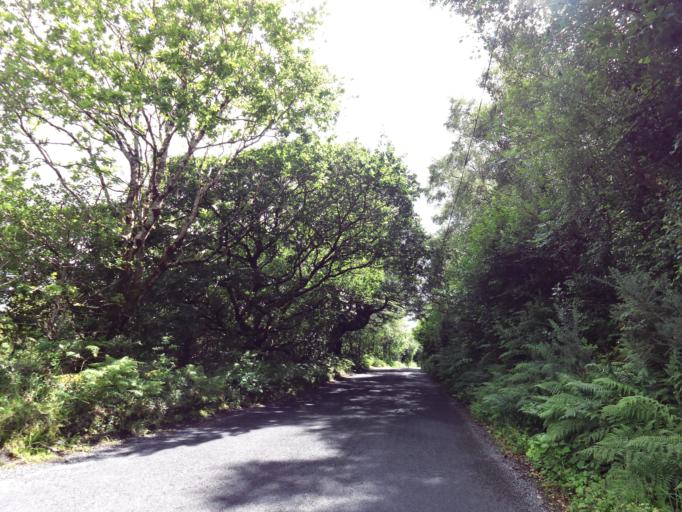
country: IE
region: Connaught
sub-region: County Galway
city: Oughterard
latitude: 53.4092
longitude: -9.3296
